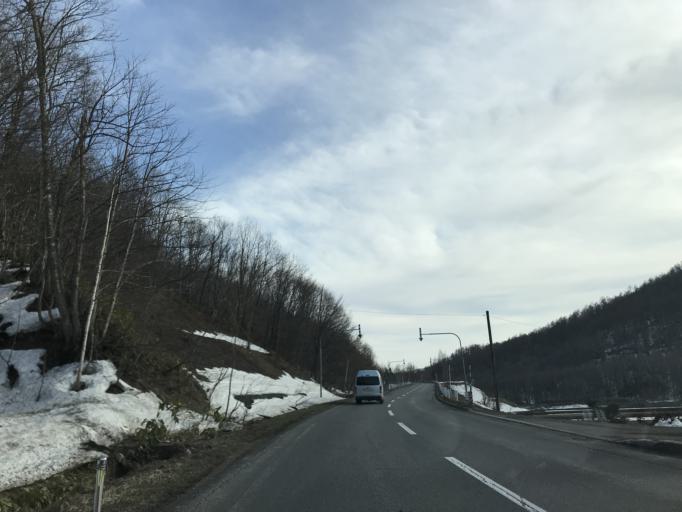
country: JP
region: Hokkaido
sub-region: Asahikawa-shi
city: Asahikawa
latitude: 43.7220
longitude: 142.3195
